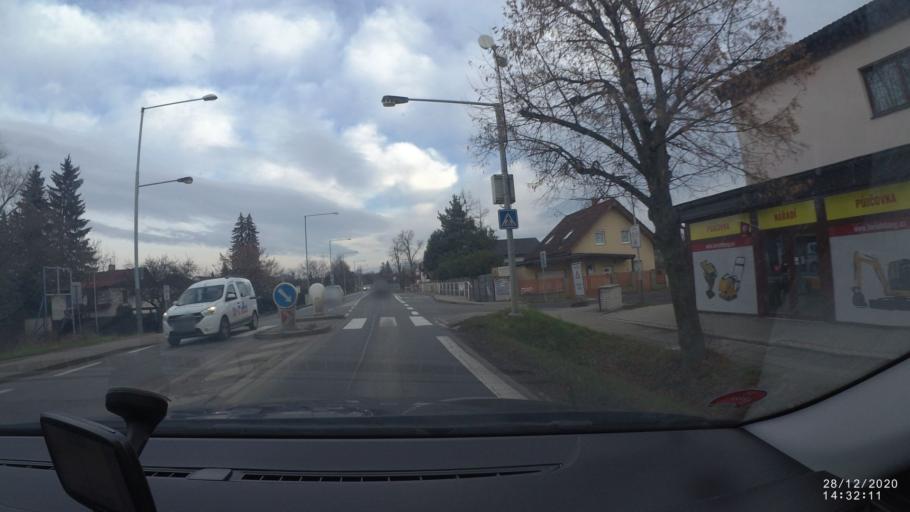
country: CZ
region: Central Bohemia
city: Sestajovice
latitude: 50.0744
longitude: 14.6708
